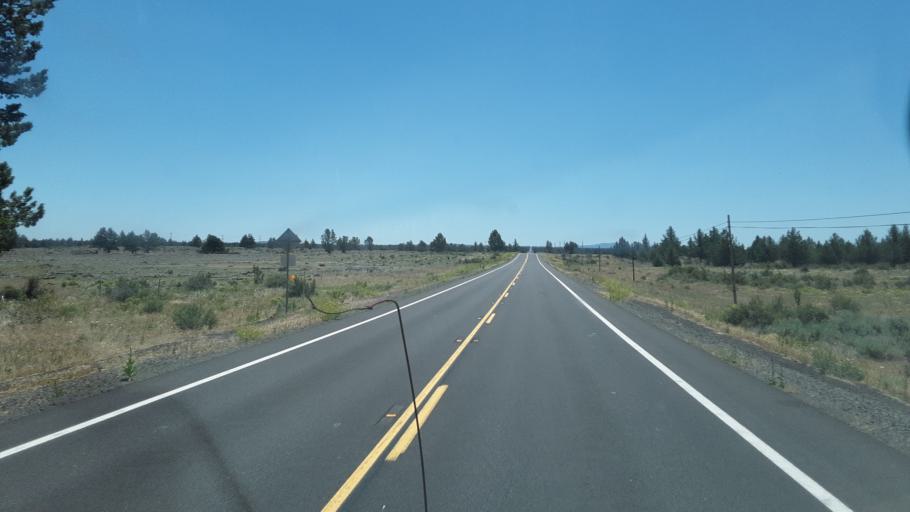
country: US
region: California
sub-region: Siskiyou County
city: Tulelake
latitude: 41.6823
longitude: -121.2660
